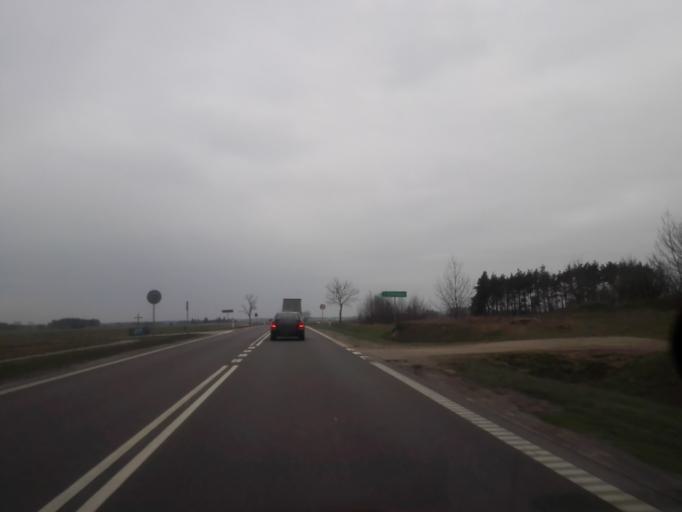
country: PL
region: Podlasie
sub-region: Powiat grajewski
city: Szczuczyn
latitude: 53.5852
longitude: 22.3266
